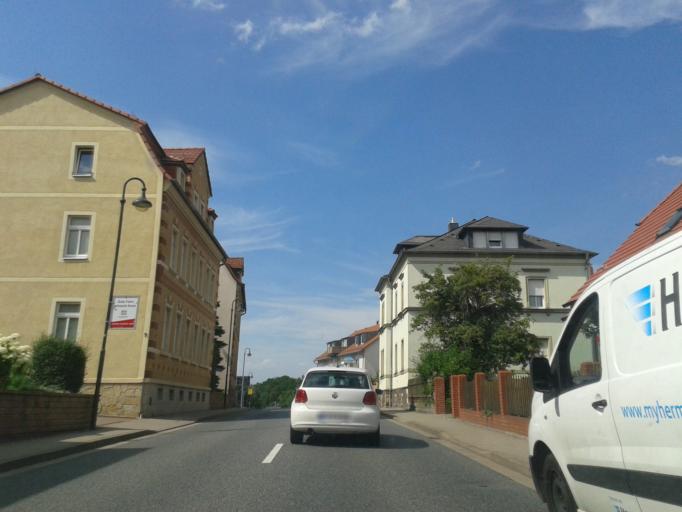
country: DE
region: Saxony
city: Wilsdruff
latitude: 51.0520
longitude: 13.5353
